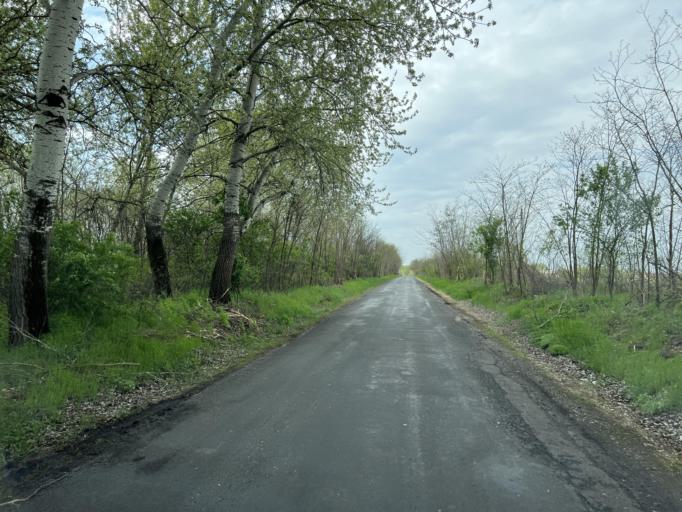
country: HU
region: Pest
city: Orkeny
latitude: 47.1331
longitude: 19.4589
